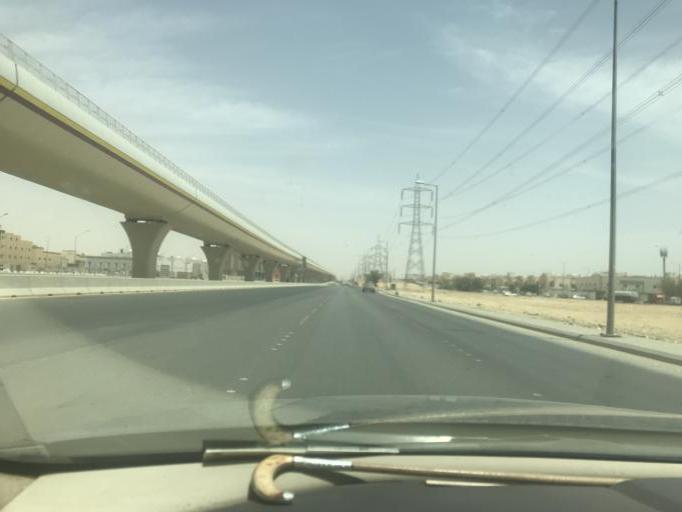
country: SA
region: Ar Riyad
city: Riyadh
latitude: 24.7896
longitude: 46.6685
